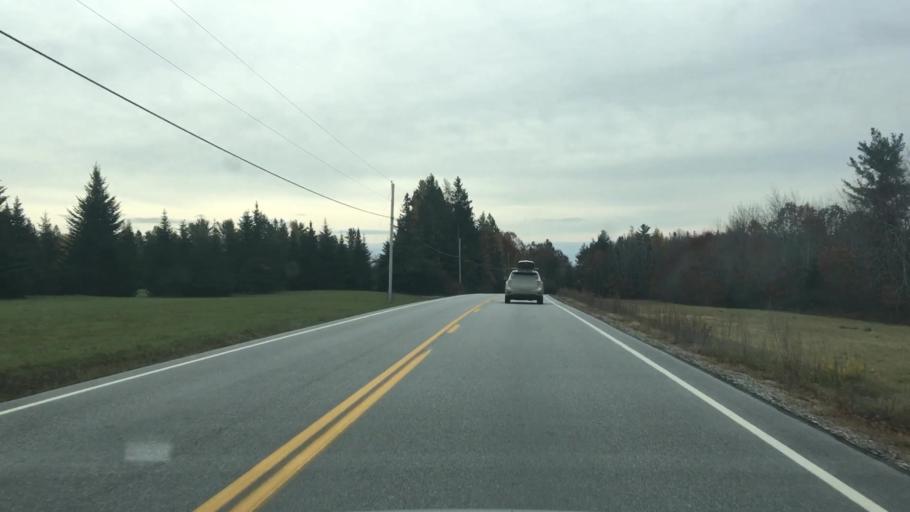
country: US
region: Maine
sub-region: Hancock County
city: Penobscot
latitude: 44.4788
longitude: -68.6385
